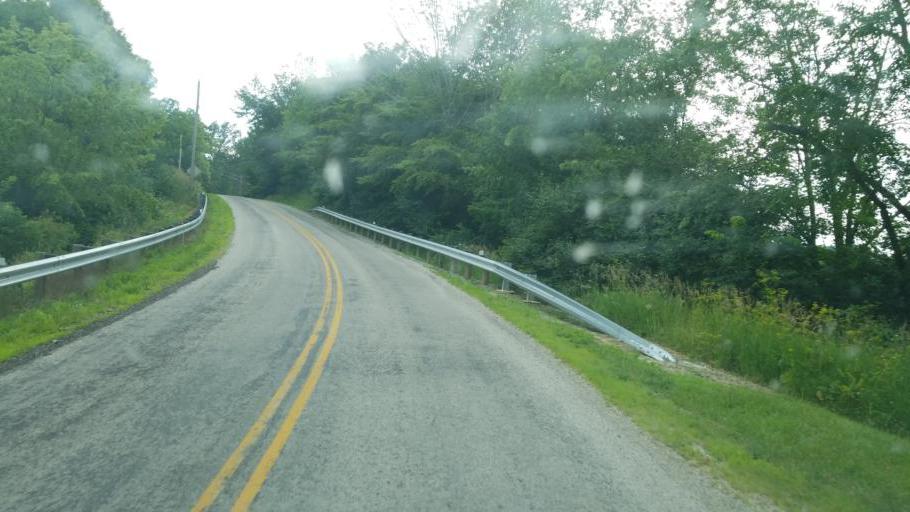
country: US
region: Ohio
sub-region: Ashland County
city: Ashland
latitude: 40.7717
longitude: -82.2242
